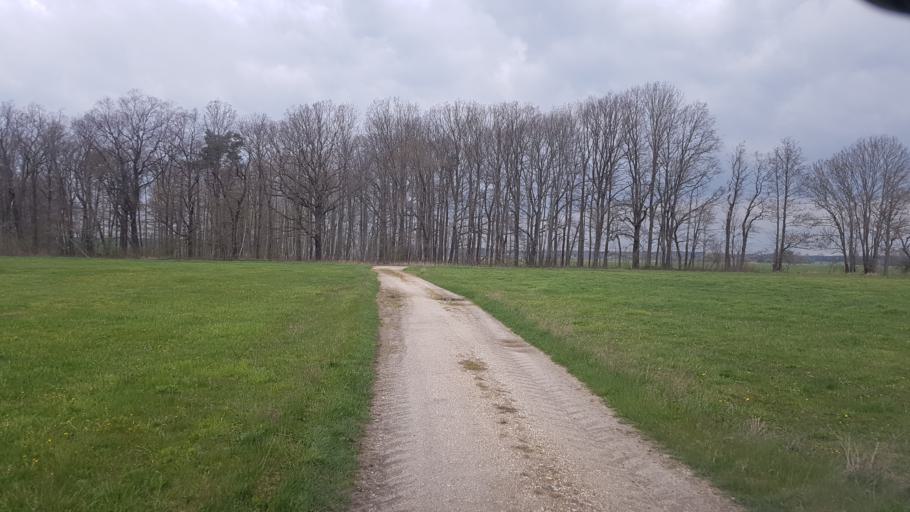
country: DE
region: Brandenburg
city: Sallgast
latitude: 51.6242
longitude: 13.8741
